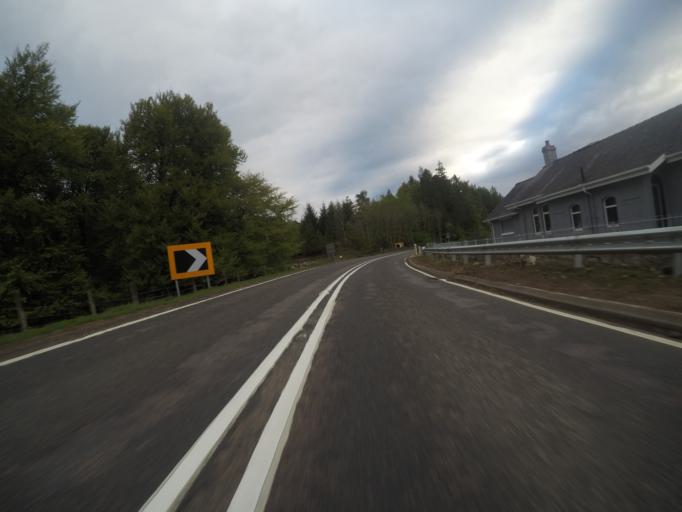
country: GB
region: Scotland
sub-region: Highland
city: Spean Bridge
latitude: 57.0367
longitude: -4.8121
